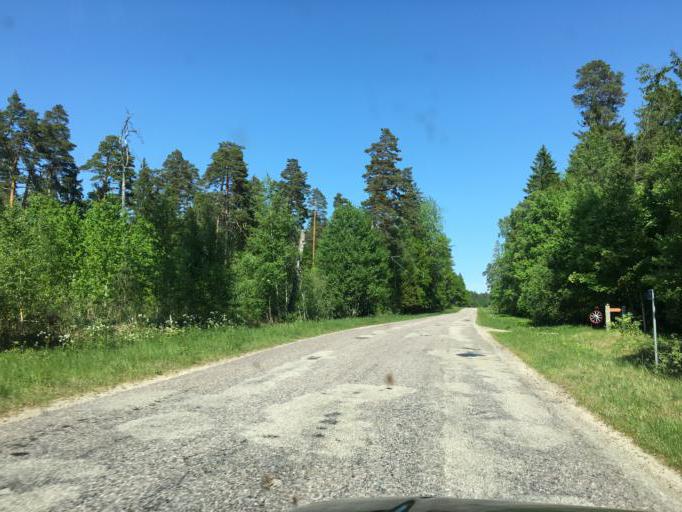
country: LV
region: Dundaga
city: Dundaga
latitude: 57.4768
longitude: 22.3249
